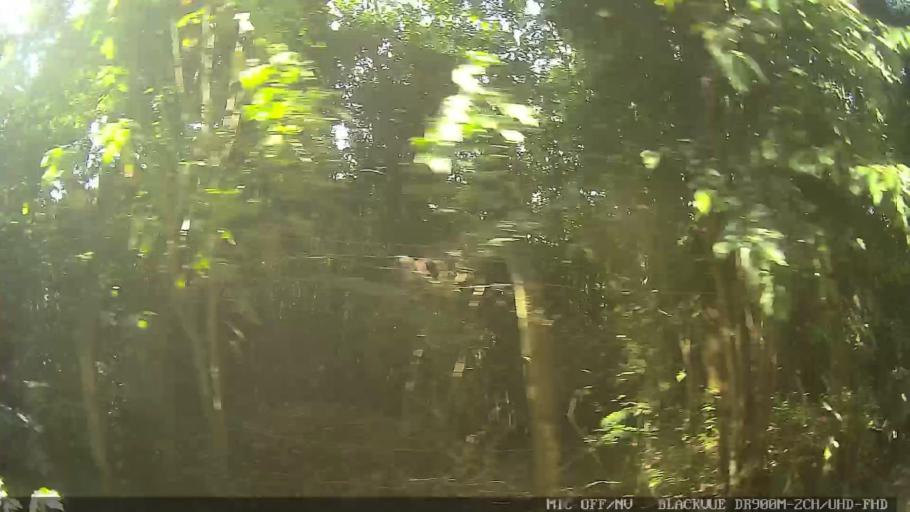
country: BR
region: Minas Gerais
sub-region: Extrema
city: Extrema
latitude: -22.8474
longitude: -46.2578
